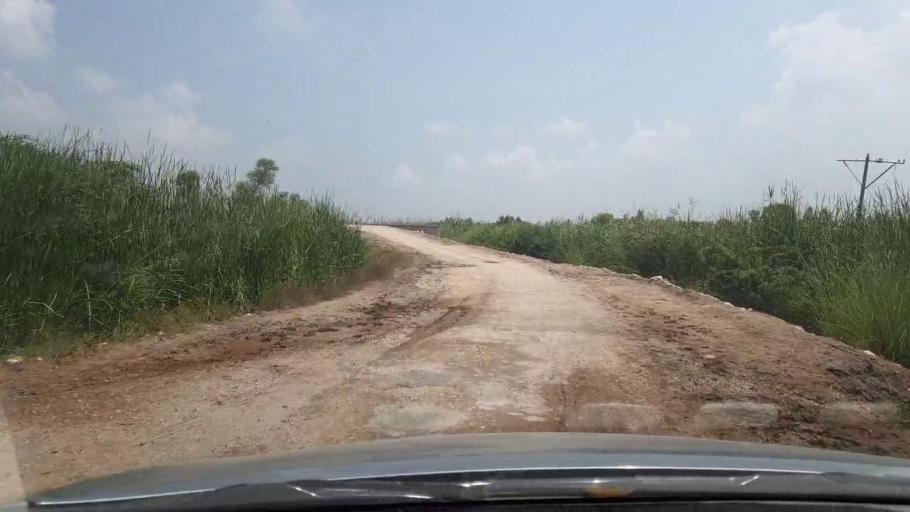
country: PK
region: Sindh
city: Khairpur
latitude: 27.4814
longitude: 68.7090
